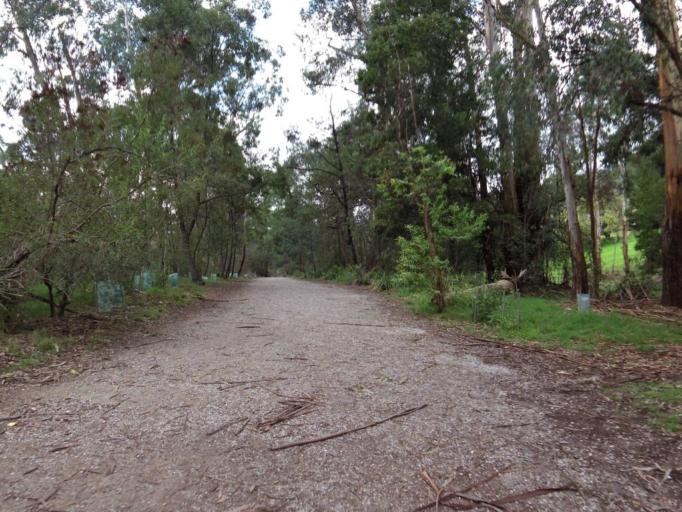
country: AU
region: Victoria
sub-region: Nillumbik
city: North Warrandyte
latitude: -37.7397
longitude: 145.2147
